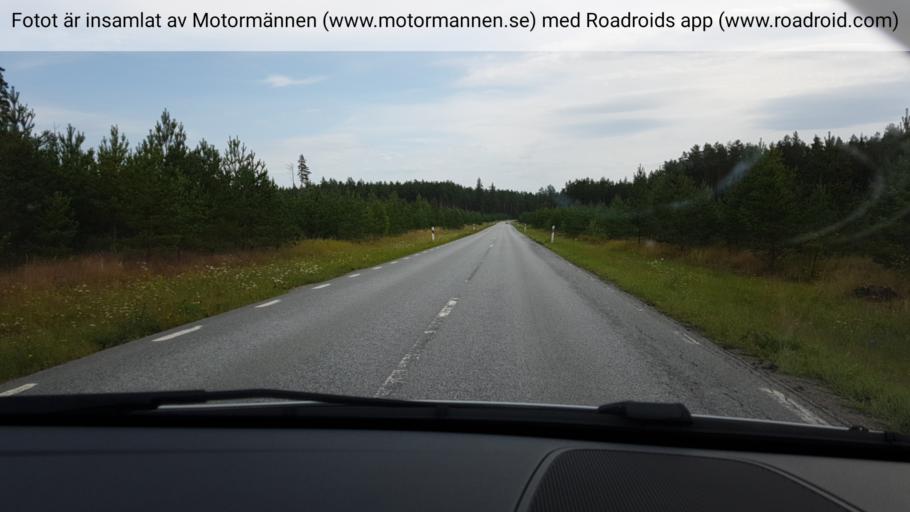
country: SE
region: Uppsala
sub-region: Osthammars Kommun
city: OEsthammar
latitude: 60.2100
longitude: 18.3679
